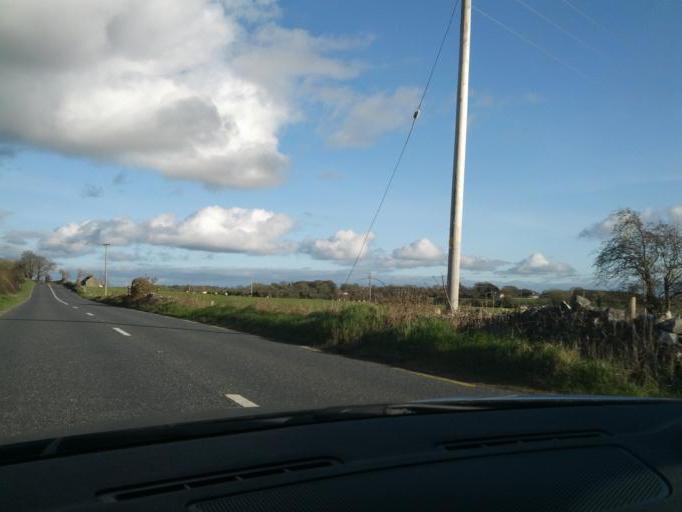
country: IE
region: Connaught
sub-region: Roscommon
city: Roscommon
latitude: 53.6671
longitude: -8.3108
